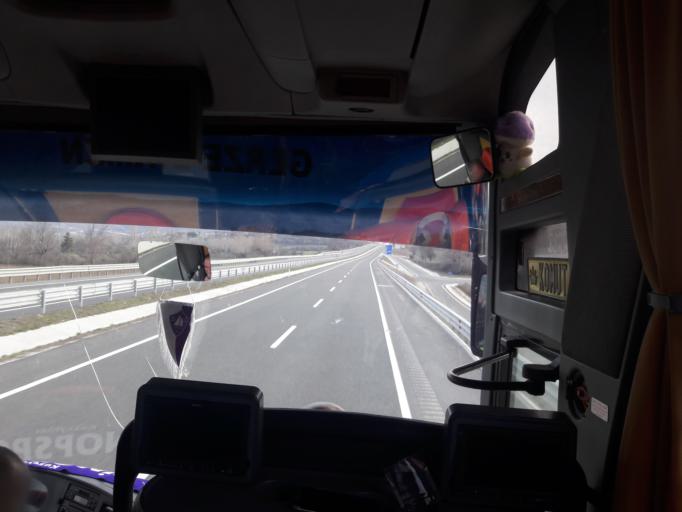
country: TR
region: Cankiri
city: Ilgaz
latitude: 40.9363
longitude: 33.6552
